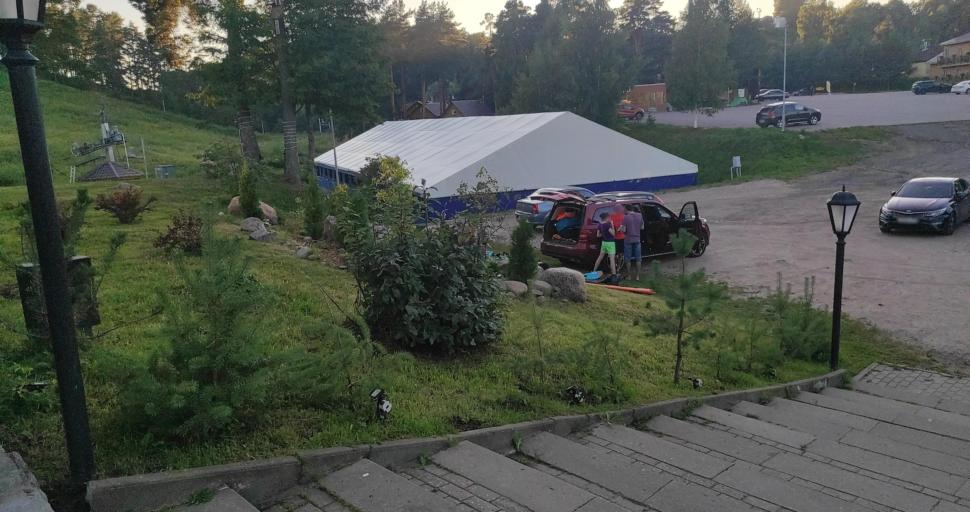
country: RU
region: Leningrad
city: Toksovo
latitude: 60.1555
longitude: 30.5498
